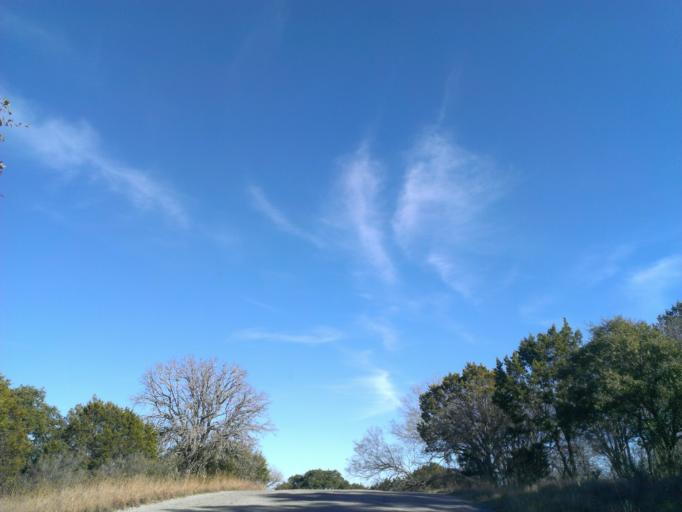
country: US
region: Texas
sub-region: Llano County
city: Horseshoe Bay
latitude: 30.5409
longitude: -98.3383
